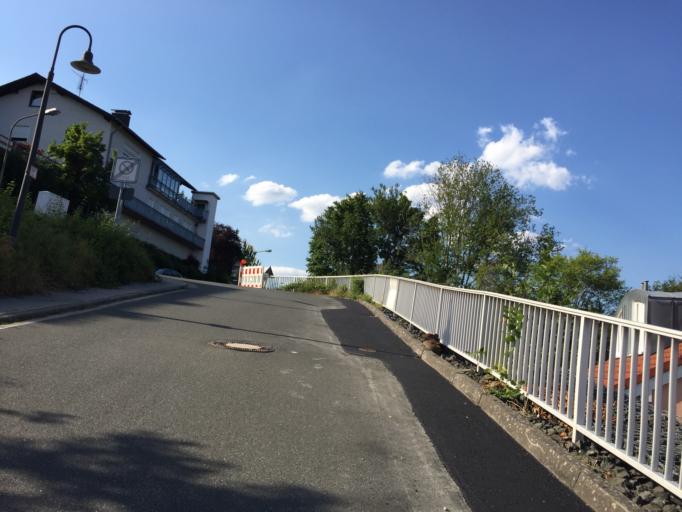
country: DE
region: Hesse
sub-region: Regierungsbezirk Giessen
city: Heuchelheim
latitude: 50.6151
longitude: 8.6422
